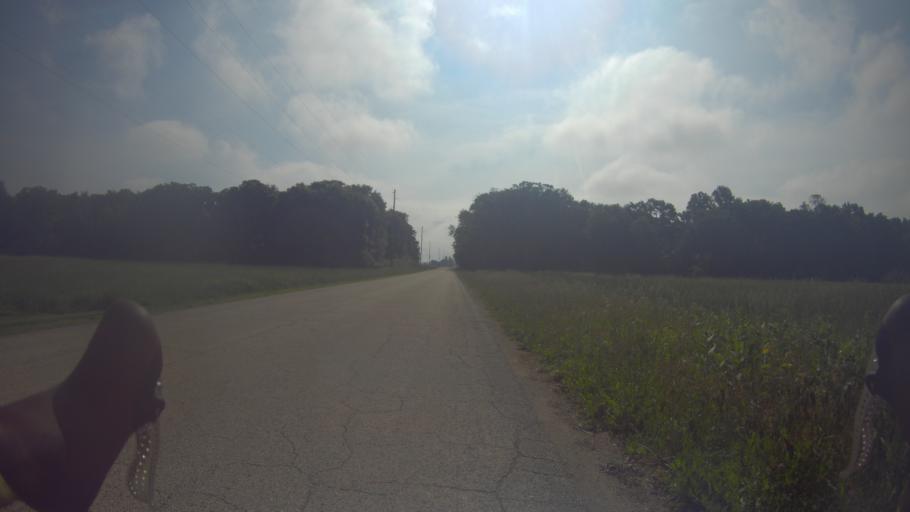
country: US
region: Wisconsin
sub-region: Dane County
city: McFarland
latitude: 42.9912
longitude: -89.2251
